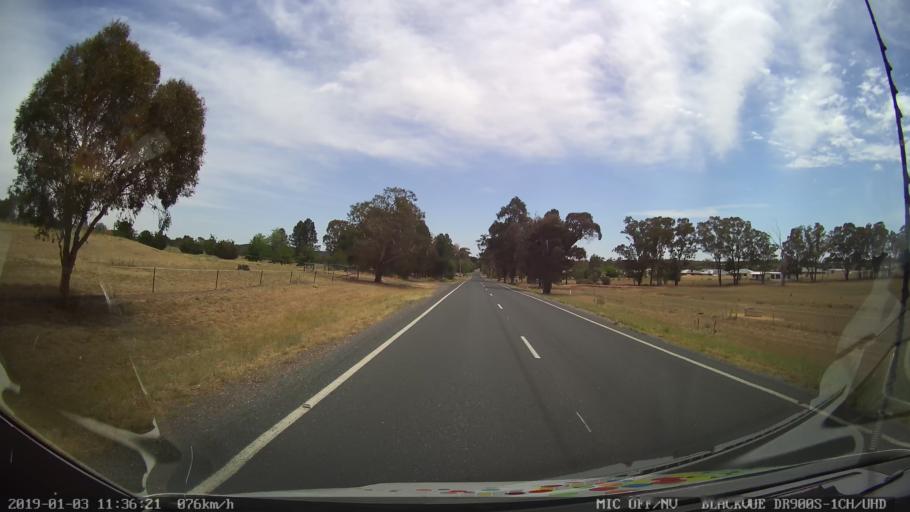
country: AU
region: New South Wales
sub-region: Weddin
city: Grenfell
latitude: -33.9116
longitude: 148.1597
